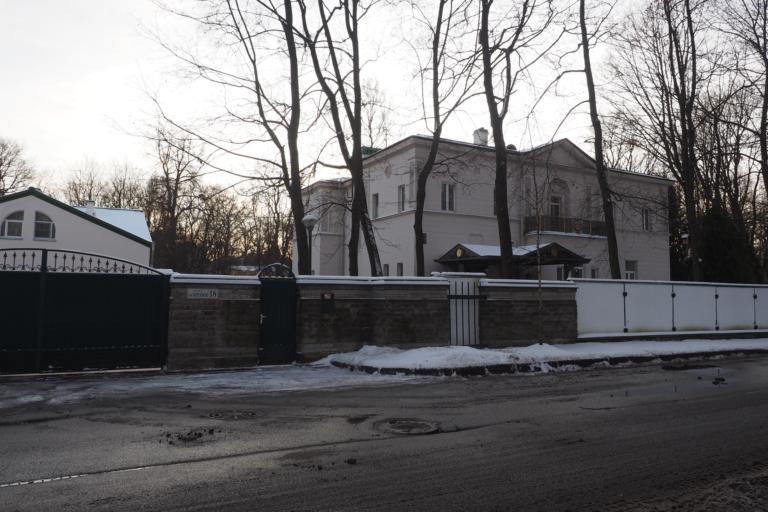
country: RU
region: St.-Petersburg
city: Novaya Derevnya
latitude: 59.9782
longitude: 30.2930
